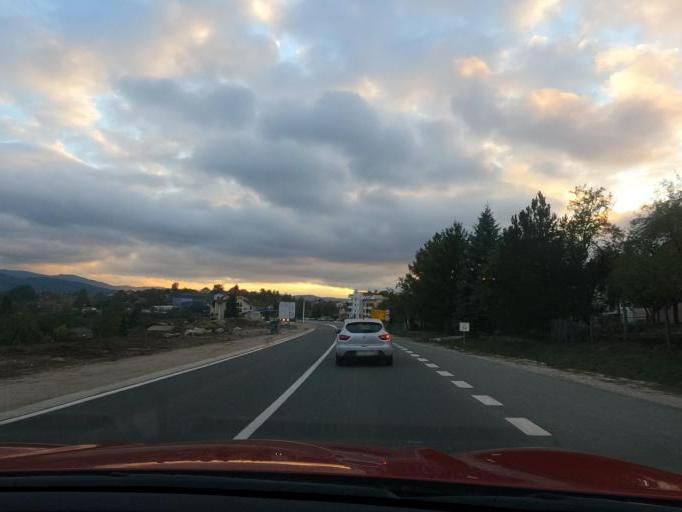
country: RS
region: Central Serbia
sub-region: Zlatiborski Okrug
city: Uzice
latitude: 43.8123
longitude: 19.7933
